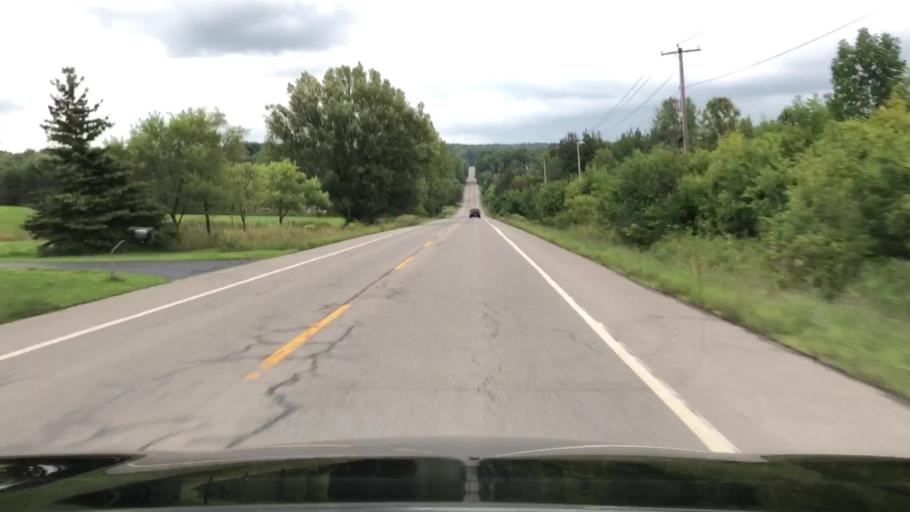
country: US
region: New York
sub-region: Erie County
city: Orchard Park
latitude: 42.7653
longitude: -78.6969
